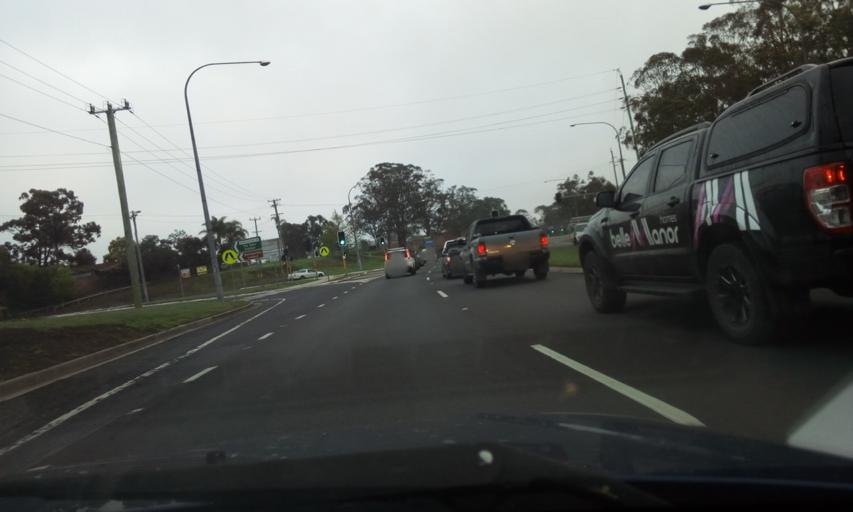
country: AU
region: New South Wales
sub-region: Camden
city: Camden South
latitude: -34.0767
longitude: 150.6948
